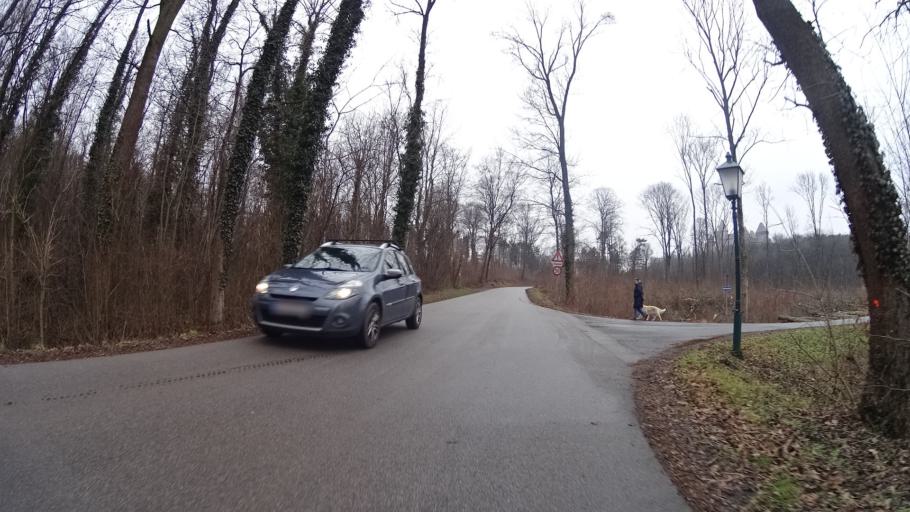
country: AT
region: Lower Austria
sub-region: Politischer Bezirk Korneuburg
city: Leobendorf
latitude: 48.3744
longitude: 16.3092
